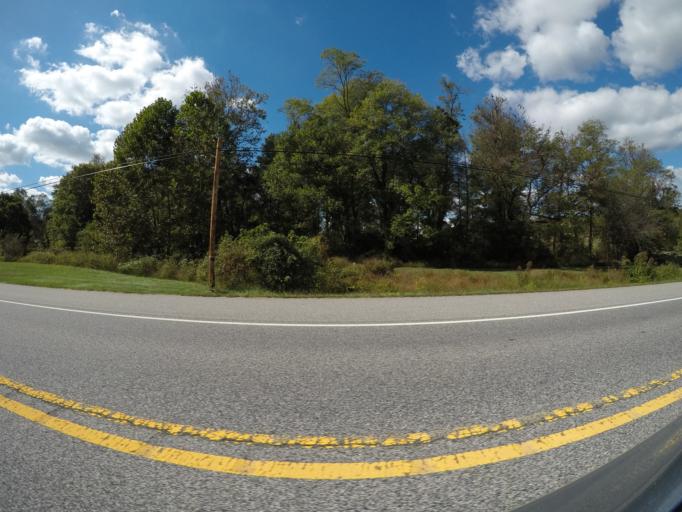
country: US
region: Pennsylvania
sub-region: York County
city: Susquehanna Trails
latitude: 39.6737
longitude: -76.2868
